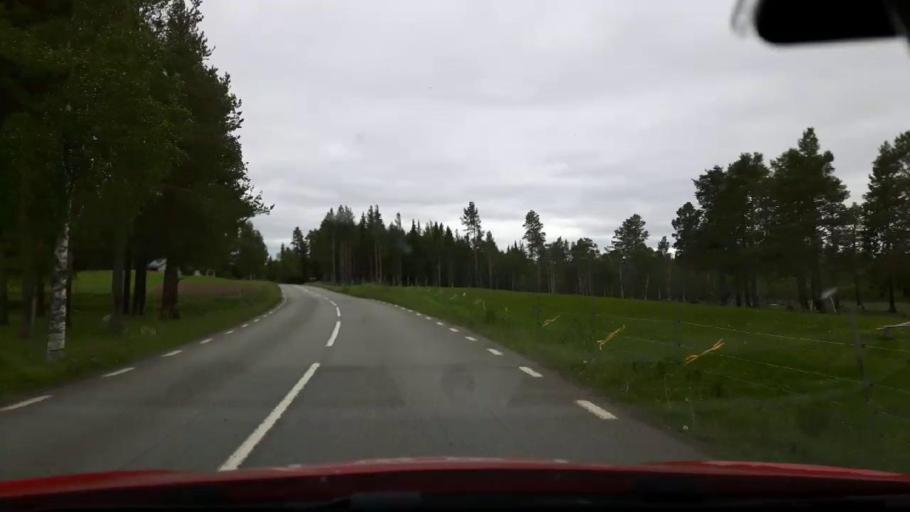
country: SE
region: Jaemtland
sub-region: Stroemsunds Kommun
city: Stroemsund
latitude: 63.4877
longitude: 15.4472
